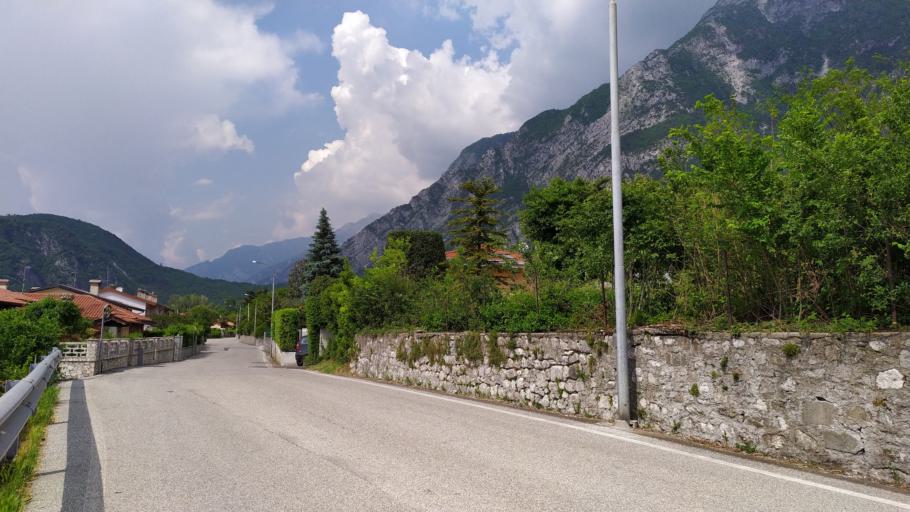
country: IT
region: Friuli Venezia Giulia
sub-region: Provincia di Udine
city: Gemona
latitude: 46.2862
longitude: 13.1380
